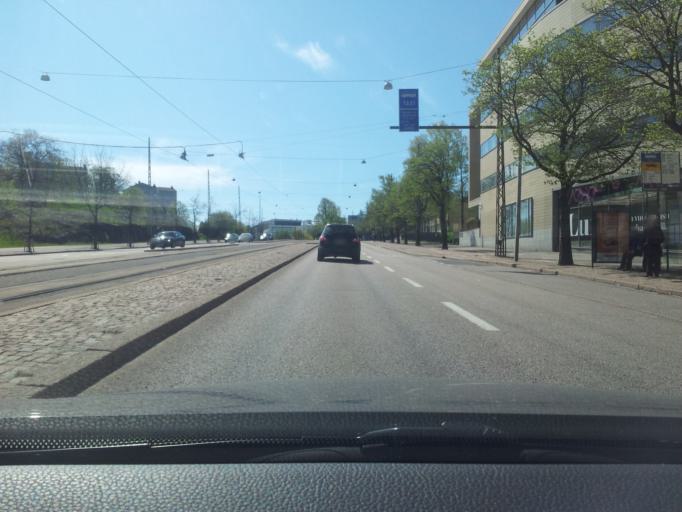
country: FI
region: Uusimaa
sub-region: Helsinki
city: Helsinki
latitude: 60.2029
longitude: 24.8992
